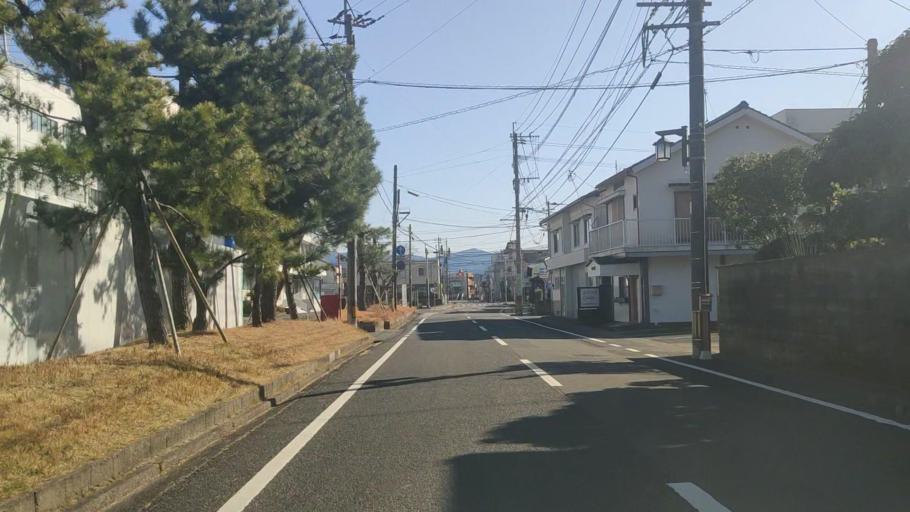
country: JP
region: Oita
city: Saiki
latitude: 32.9606
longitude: 131.8961
